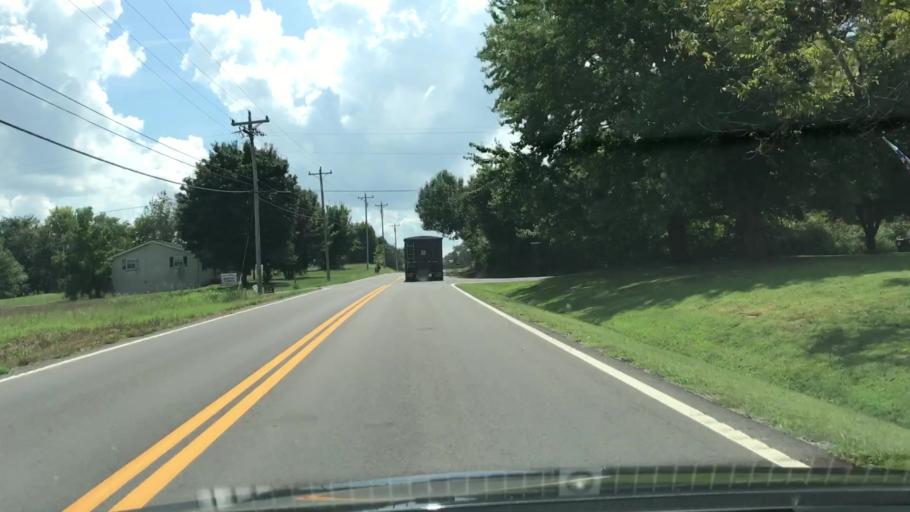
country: US
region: Tennessee
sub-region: Robertson County
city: Springfield
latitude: 36.5998
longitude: -86.9184
